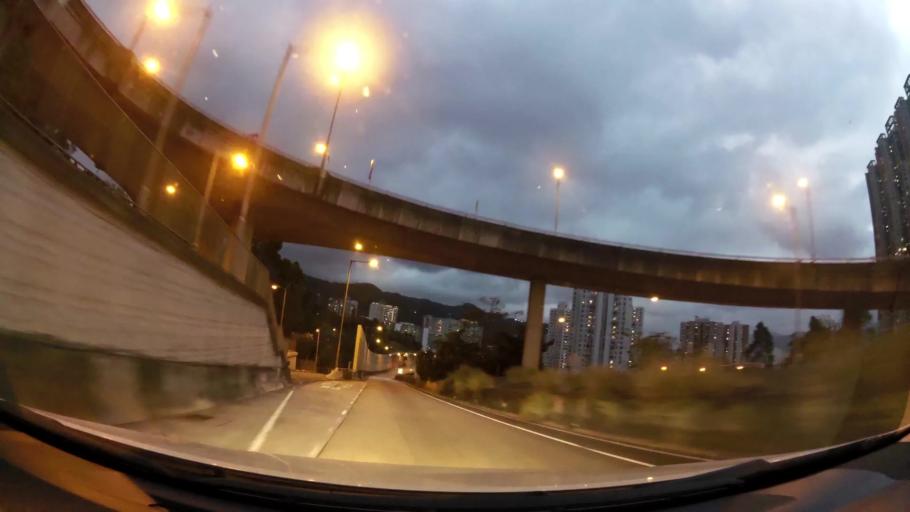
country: HK
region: Sha Tin
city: Sha Tin
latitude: 22.3719
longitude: 114.1745
